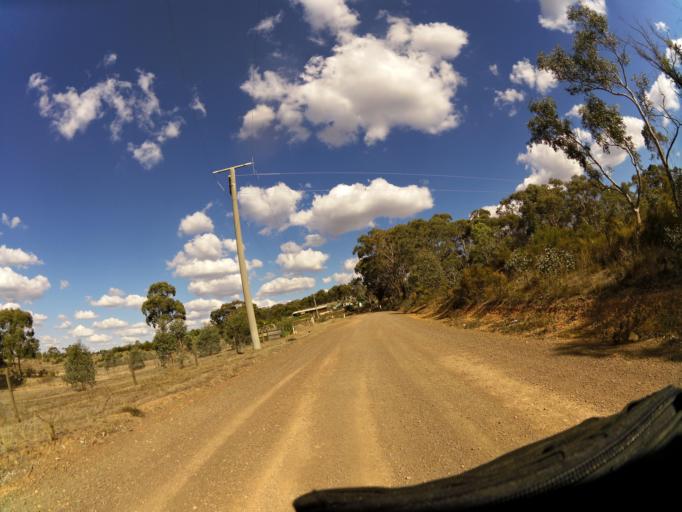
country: AU
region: Victoria
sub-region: Greater Bendigo
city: Kennington
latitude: -36.9544
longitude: 144.7768
